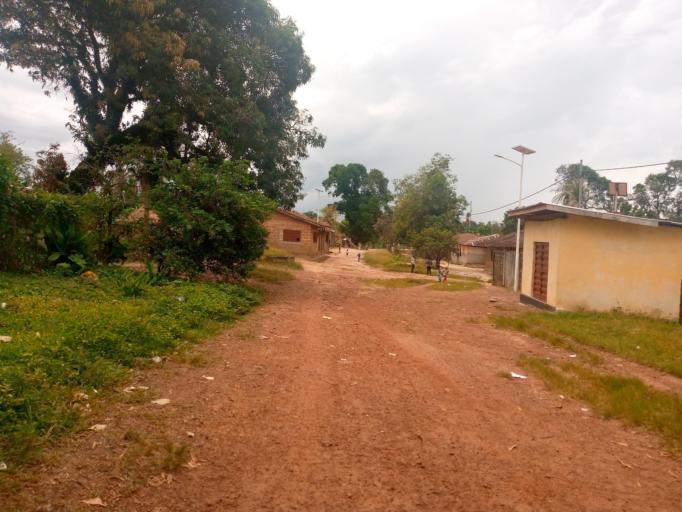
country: SL
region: Southern Province
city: Mogbwemo
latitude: 7.6065
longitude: -12.1757
